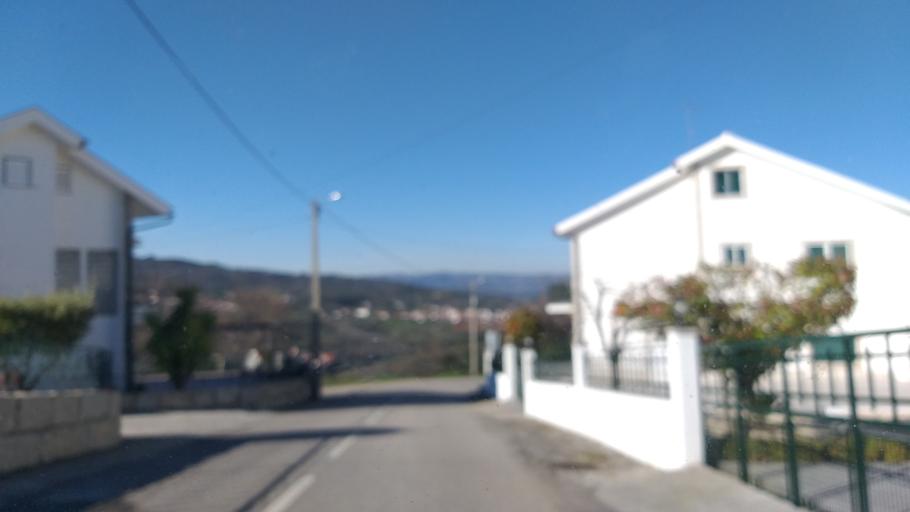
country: PT
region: Guarda
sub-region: Celorico da Beira
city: Celorico da Beira
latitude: 40.5866
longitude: -7.3605
